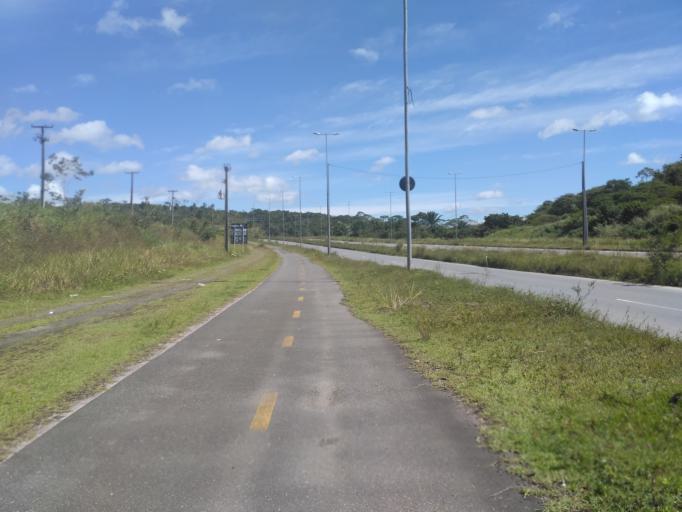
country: BR
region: Pernambuco
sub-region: Sao Lourenco Da Mata
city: Sao Lourenco da Mata
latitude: -8.0444
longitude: -34.9994
